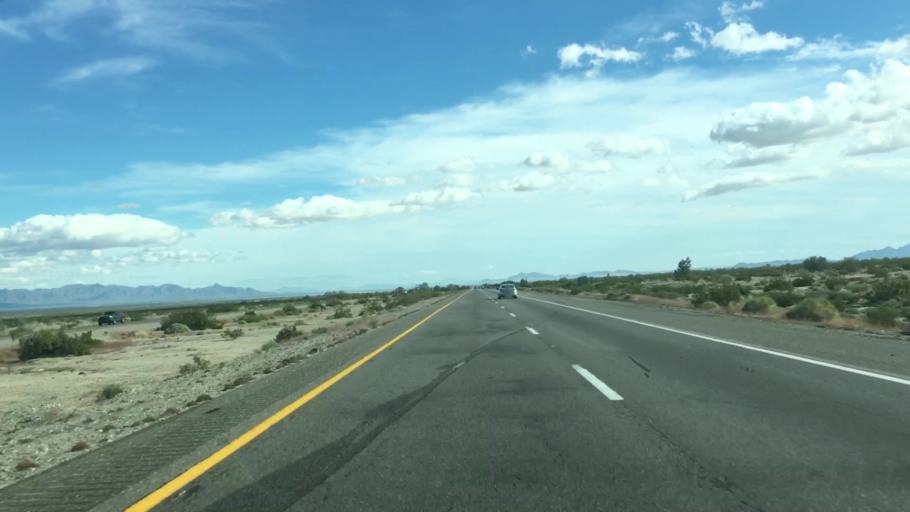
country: US
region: California
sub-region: Riverside County
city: Mesa Verde
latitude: 33.6687
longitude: -115.1978
